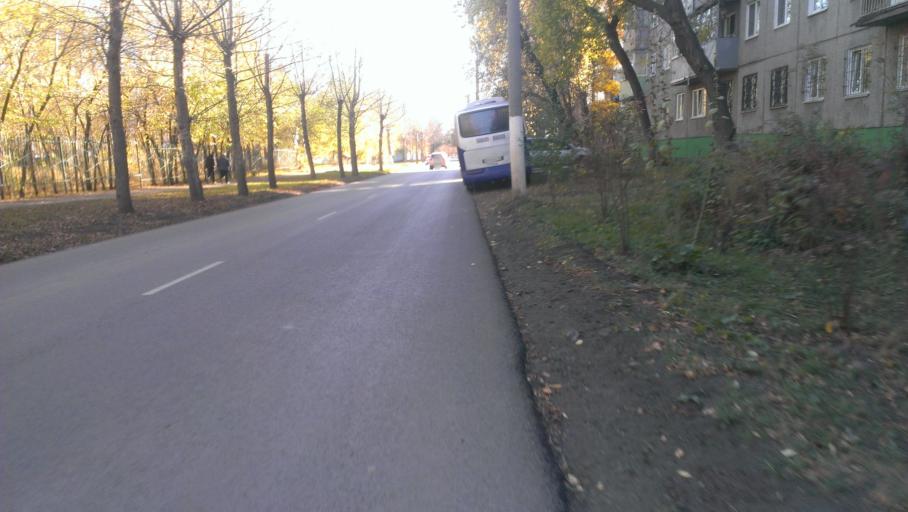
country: RU
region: Altai Krai
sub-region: Gorod Barnaulskiy
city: Barnaul
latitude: 53.3635
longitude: 83.6877
